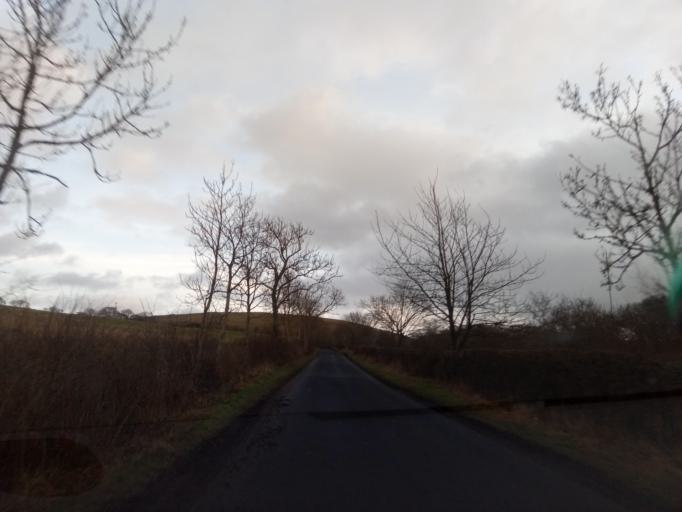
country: GB
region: Scotland
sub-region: The Scottish Borders
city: Selkirk
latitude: 55.5663
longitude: -2.8044
